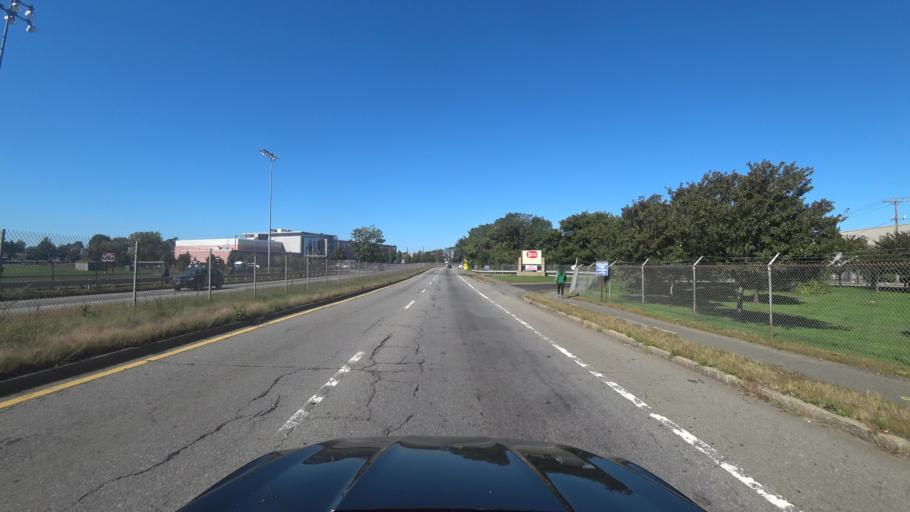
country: US
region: Massachusetts
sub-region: Suffolk County
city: Revere
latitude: 42.4120
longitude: -71.0026
